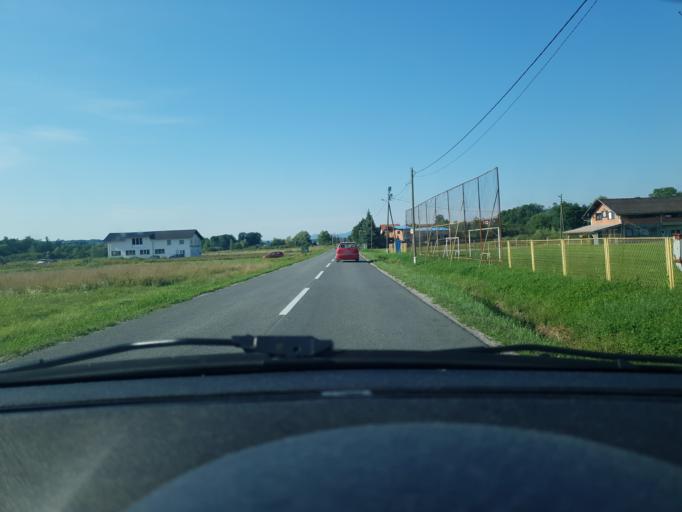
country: HR
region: Zagrebacka
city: Jakovlje
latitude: 45.9618
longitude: 15.8554
